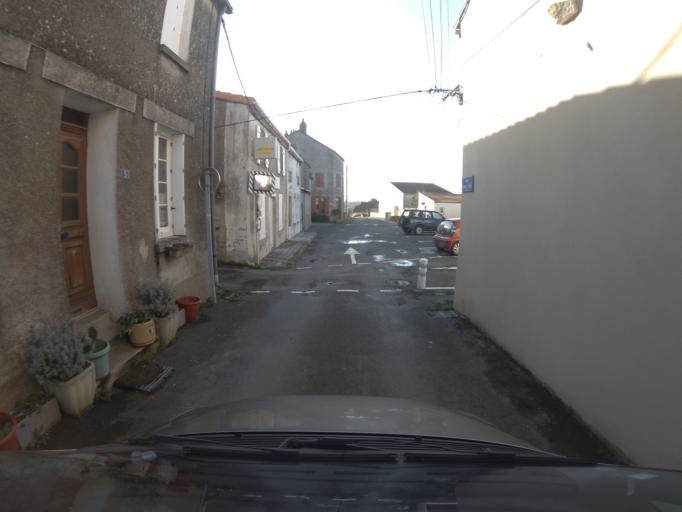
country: FR
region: Pays de la Loire
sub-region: Departement de la Loire-Atlantique
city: Remouille
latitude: 47.0547
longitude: -1.3757
